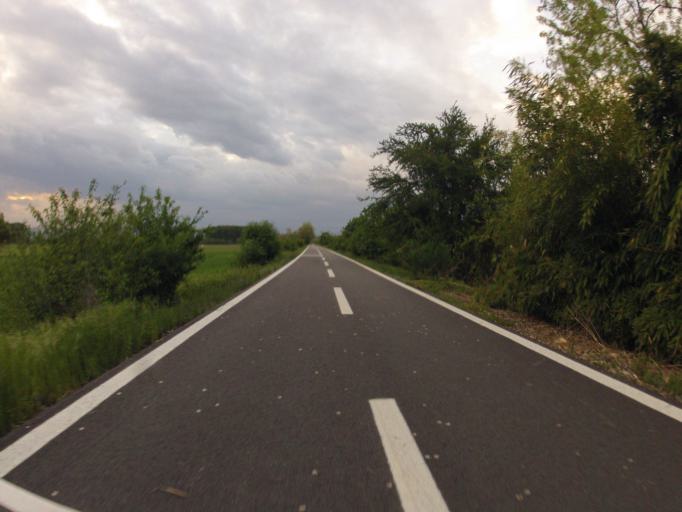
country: IT
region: Piedmont
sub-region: Provincia di Torino
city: Vigone
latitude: 44.8166
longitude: 7.4979
